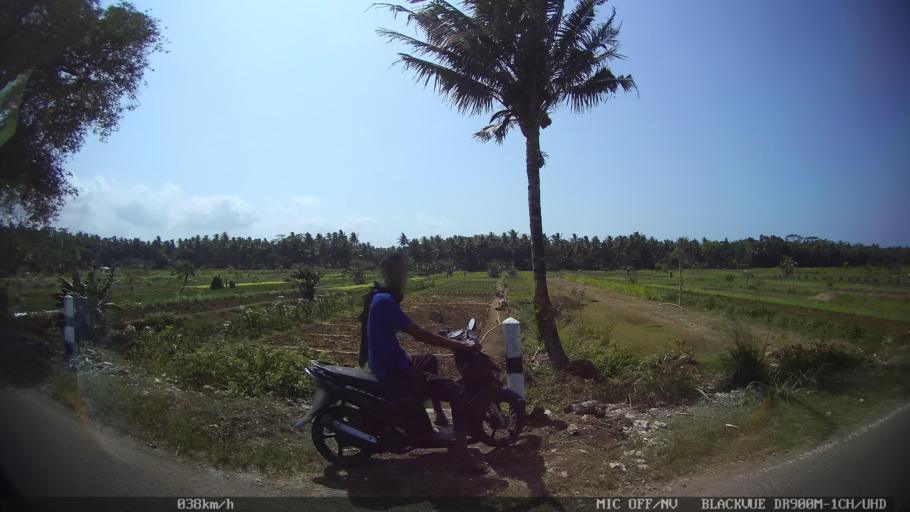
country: ID
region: Daerah Istimewa Yogyakarta
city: Srandakan
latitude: -7.9300
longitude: 110.1560
